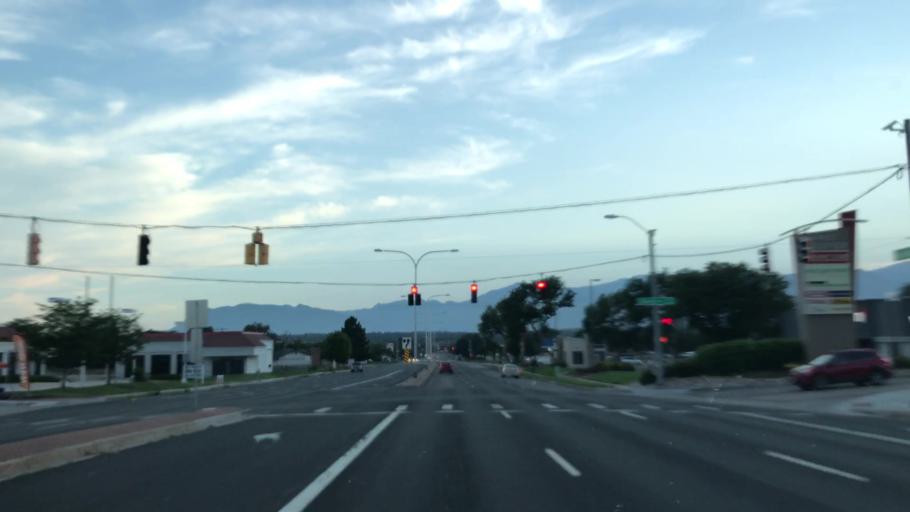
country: US
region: Colorado
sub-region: El Paso County
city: Cimarron Hills
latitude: 38.8958
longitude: -104.7493
